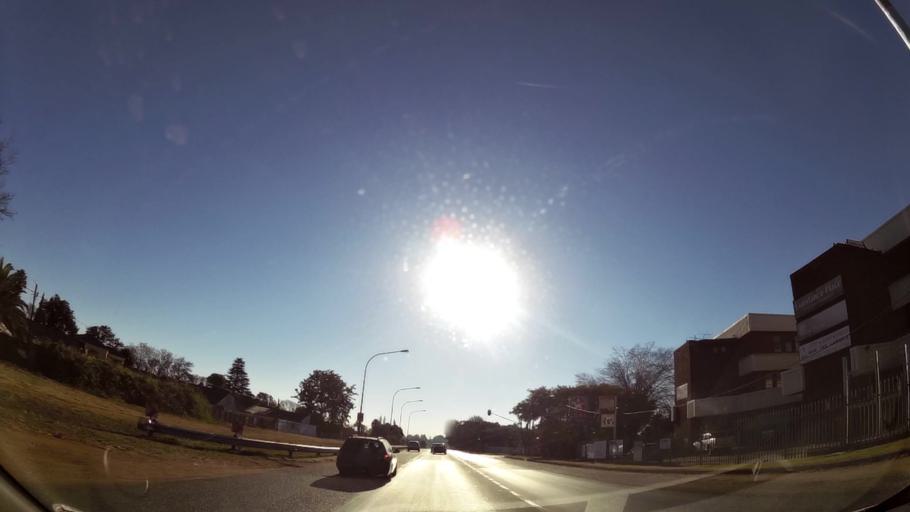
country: ZA
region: Gauteng
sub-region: Ekurhuleni Metropolitan Municipality
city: Tembisa
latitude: -26.0498
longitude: 28.2391
